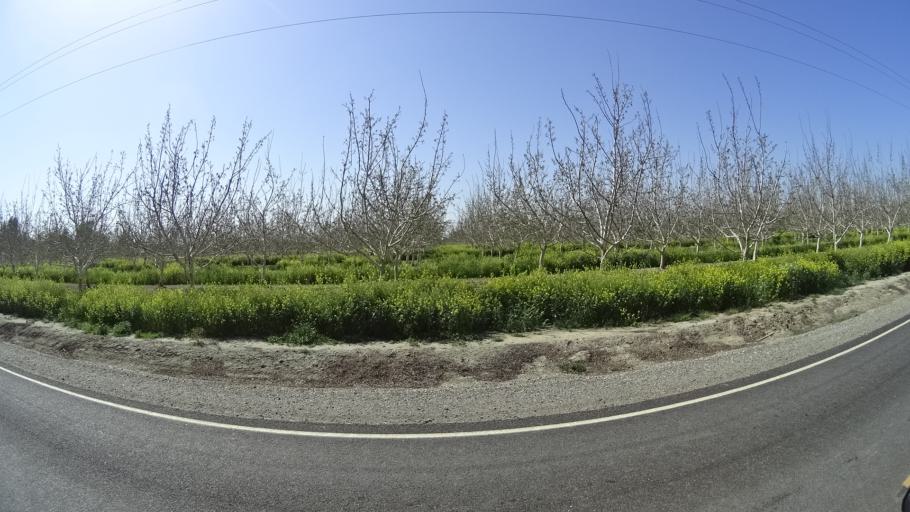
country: US
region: California
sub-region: Glenn County
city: Hamilton City
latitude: 39.6597
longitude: -122.0592
